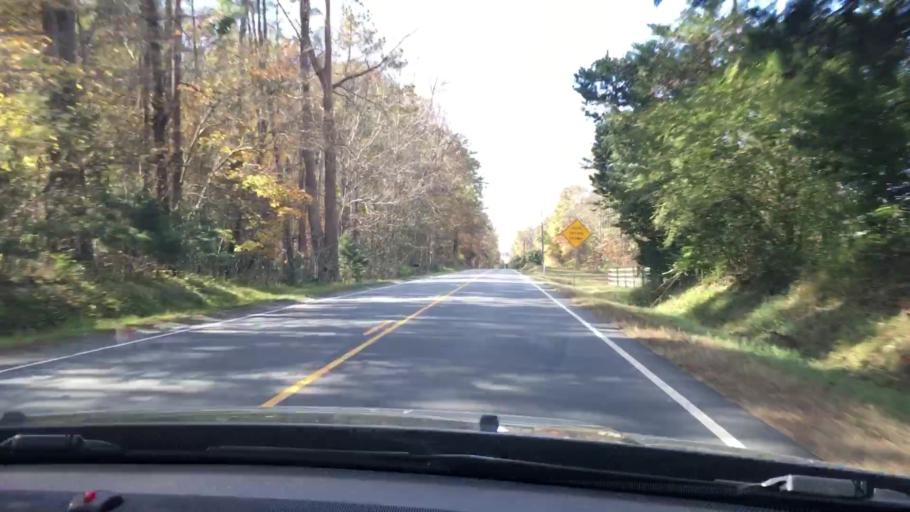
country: US
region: Virginia
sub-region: King and Queen County
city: King and Queen Court House
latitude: 37.5913
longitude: -76.8689
